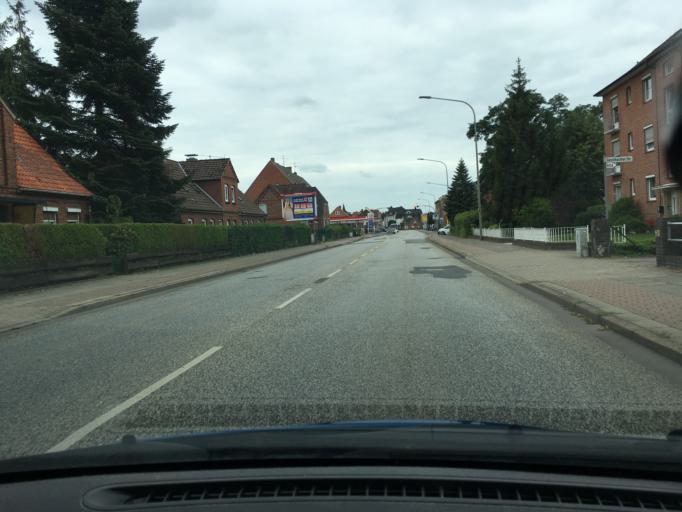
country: DE
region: Schleswig-Holstein
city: Geesthacht
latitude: 53.4459
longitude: 10.3620
